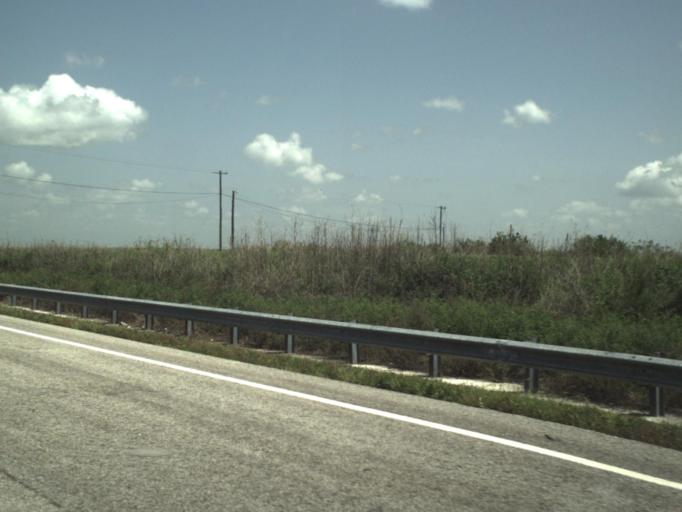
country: US
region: Florida
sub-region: Palm Beach County
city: Belle Glade Camp
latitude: 26.3843
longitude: -80.5758
